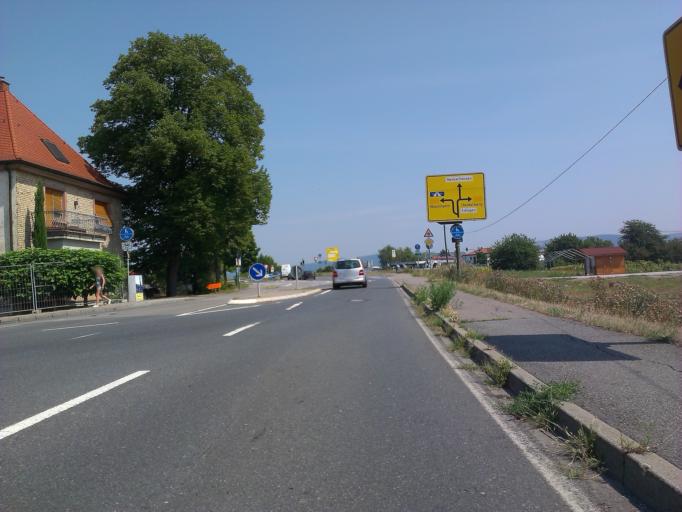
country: DE
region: Baden-Wuerttemberg
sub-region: Karlsruhe Region
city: Edingen-Neckarhausen
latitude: 49.4533
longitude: 8.5905
